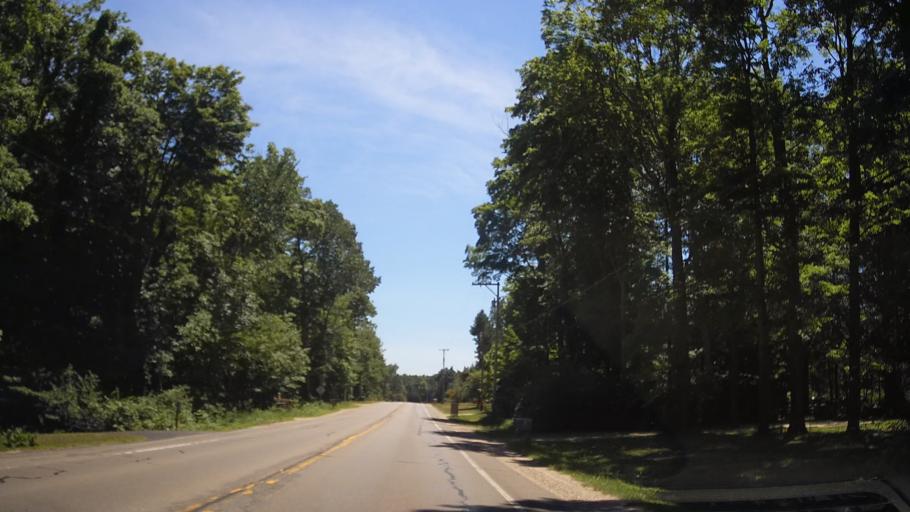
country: US
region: Michigan
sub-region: Grand Traverse County
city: Traverse City
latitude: 44.6903
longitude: -85.6904
